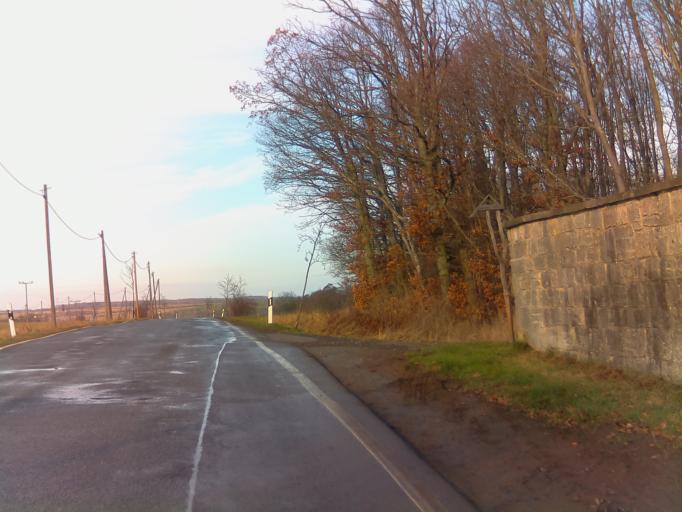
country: DE
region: Thuringia
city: Bad Berka
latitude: 50.9196
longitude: 11.2803
